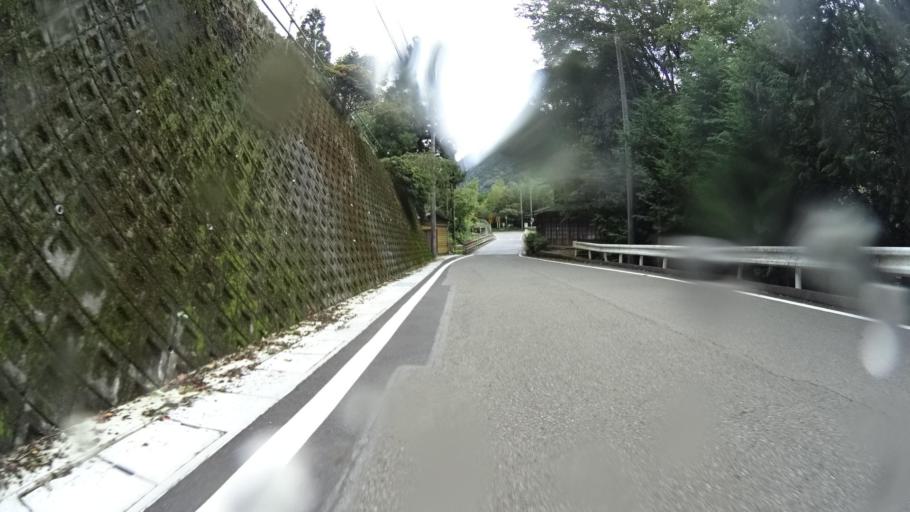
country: JP
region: Yamanashi
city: Uenohara
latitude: 35.6832
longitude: 139.0609
